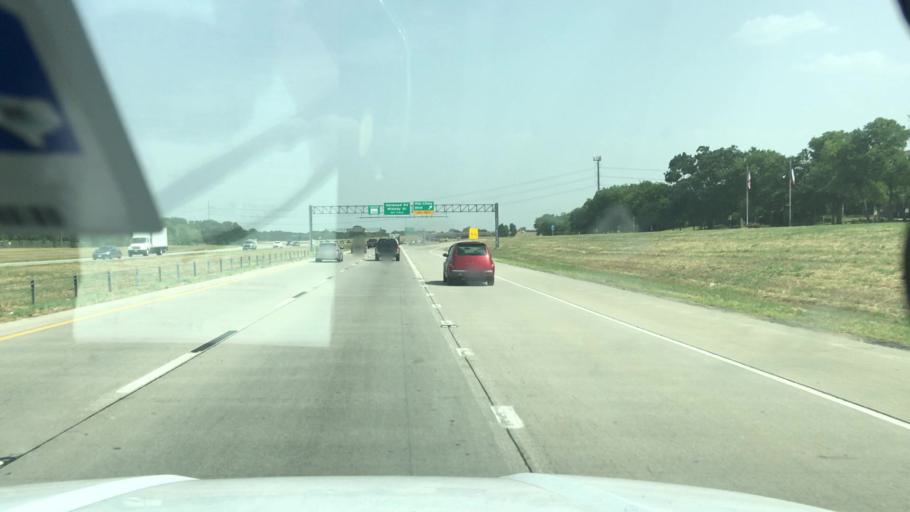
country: US
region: Texas
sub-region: Tarrant County
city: Euless
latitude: 32.8738
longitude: -97.0704
